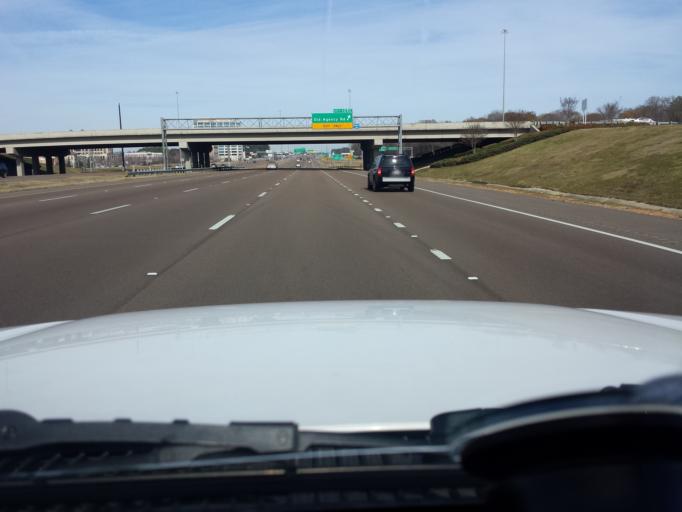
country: US
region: Mississippi
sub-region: Madison County
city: Ridgeland
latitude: 32.4297
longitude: -90.1438
